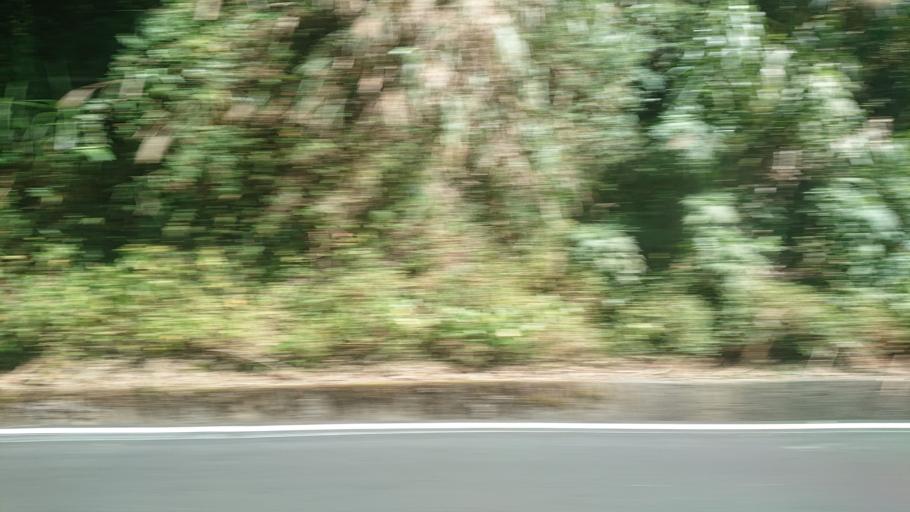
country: TW
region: Taiwan
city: Lugu
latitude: 23.4857
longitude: 120.8256
